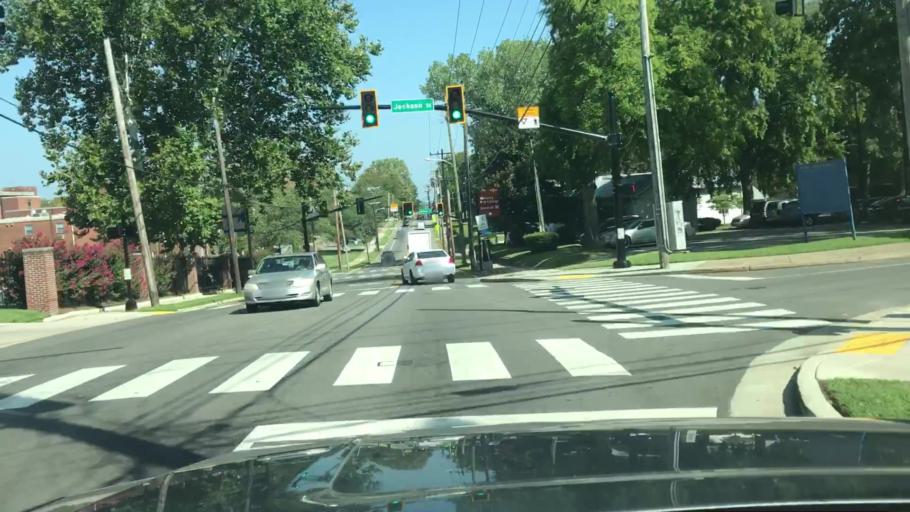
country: US
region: Tennessee
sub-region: Davidson County
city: Nashville
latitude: 36.1656
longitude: -86.8051
